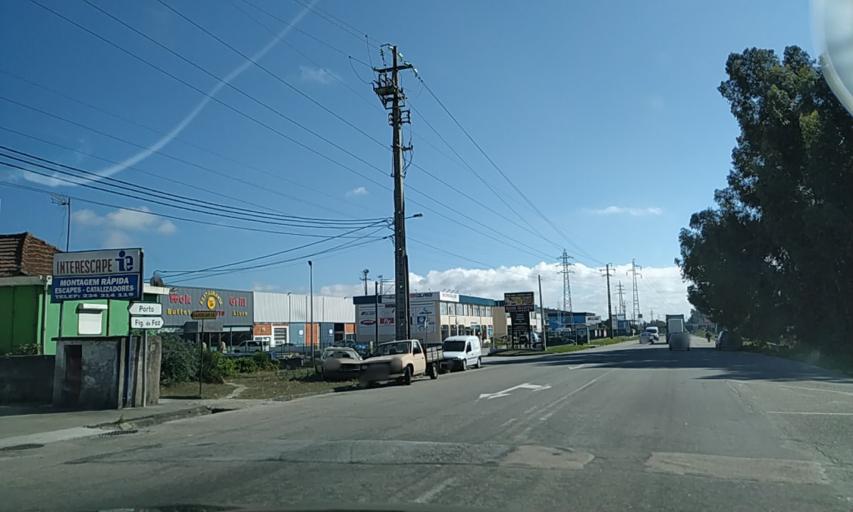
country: PT
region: Aveiro
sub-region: Aveiro
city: Aveiro
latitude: 40.6589
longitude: -8.6151
